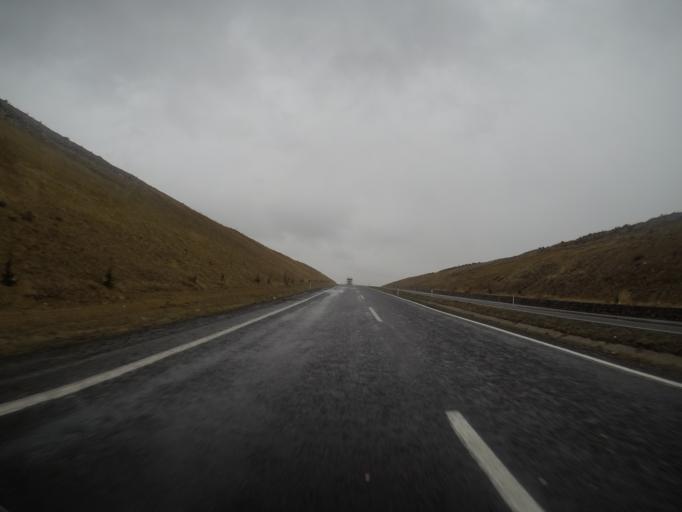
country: TR
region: Nevsehir
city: Urgub
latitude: 38.7417
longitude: 35.0132
